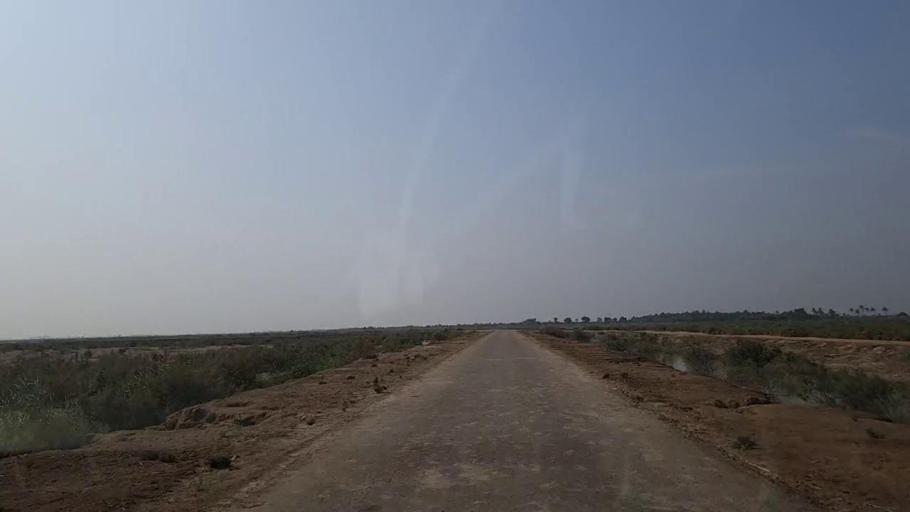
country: PK
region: Sindh
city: Gharo
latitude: 24.6732
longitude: 67.6985
